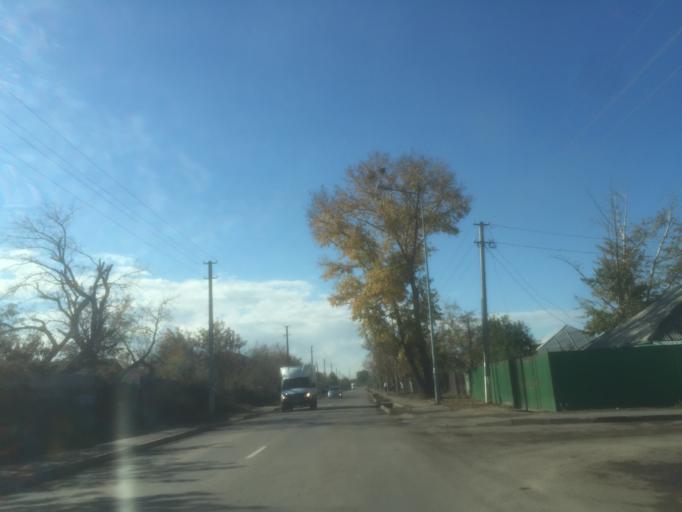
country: KZ
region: Astana Qalasy
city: Astana
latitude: 51.2020
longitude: 71.3717
